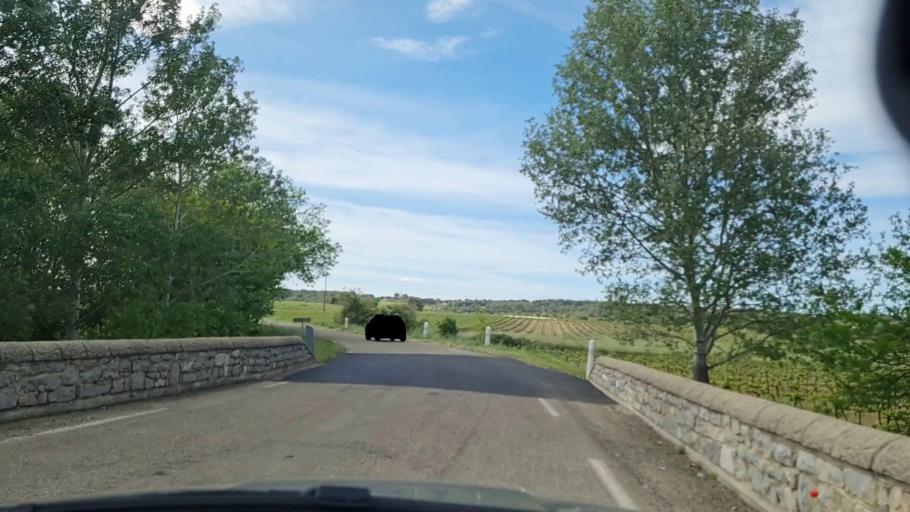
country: FR
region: Languedoc-Roussillon
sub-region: Departement du Gard
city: Villevieille
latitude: 43.8262
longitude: 4.1248
